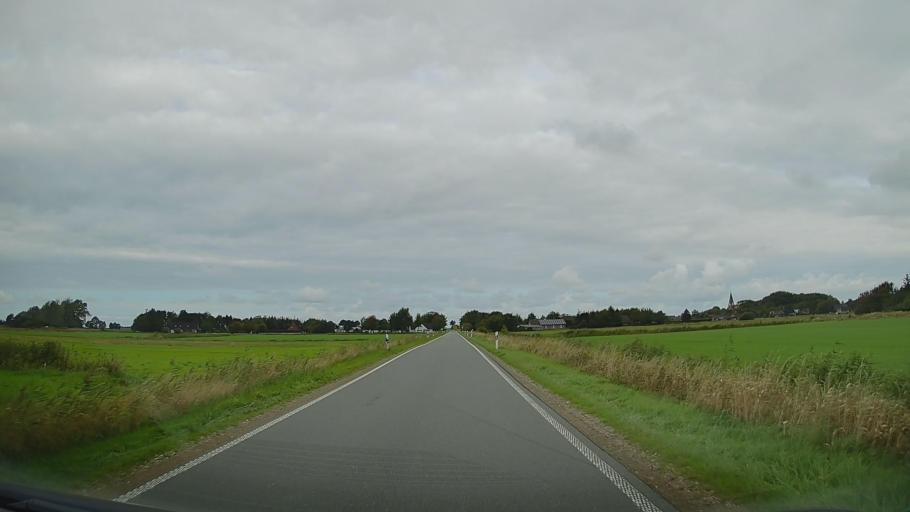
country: DE
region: Schleswig-Holstein
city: Aventoft
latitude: 54.8961
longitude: 8.8077
